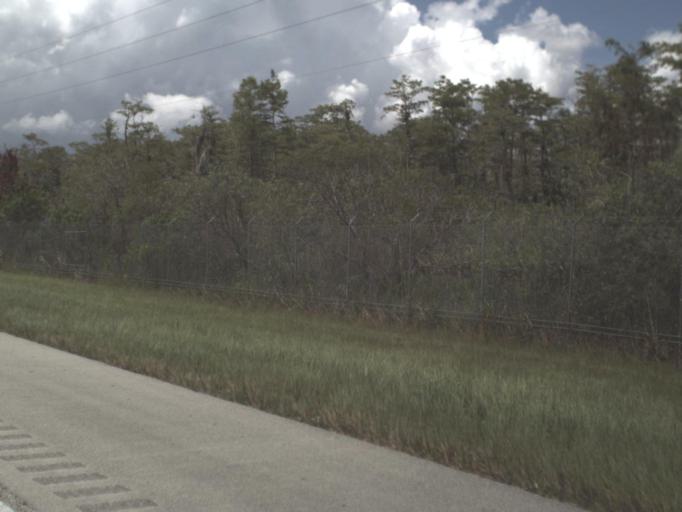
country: US
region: Florida
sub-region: Collier County
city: Immokalee
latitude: 26.1556
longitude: -81.2764
